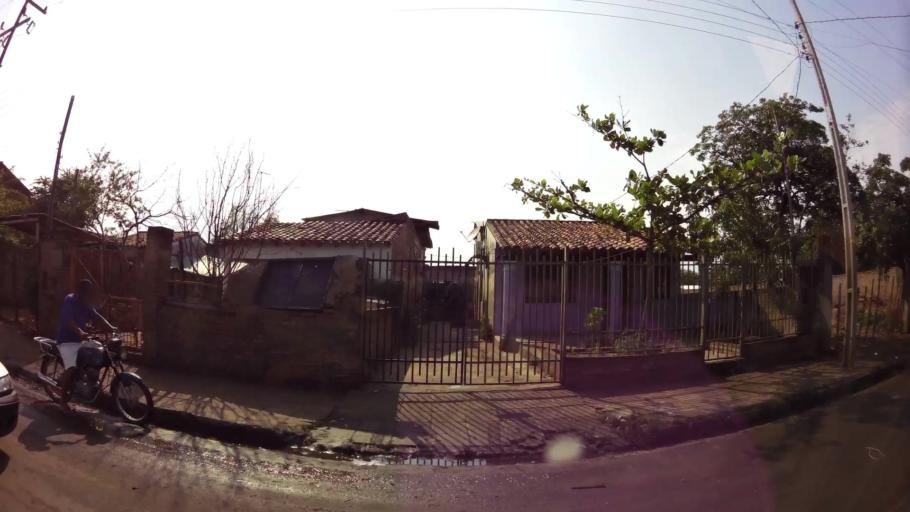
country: PY
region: Asuncion
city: Asuncion
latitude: -25.3069
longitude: -57.6674
